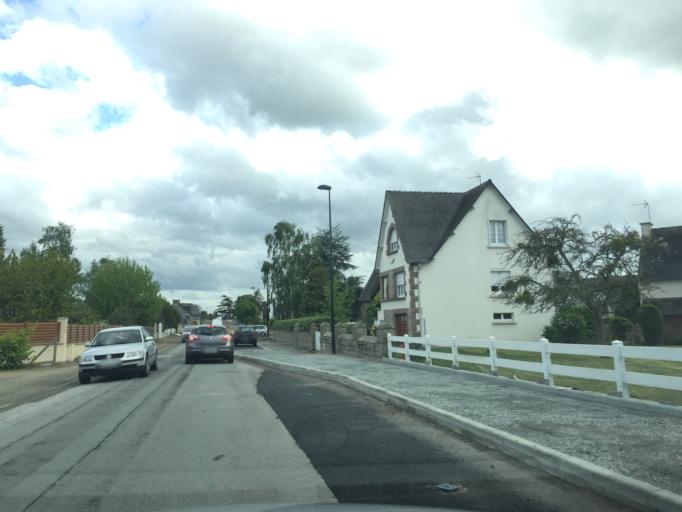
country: FR
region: Brittany
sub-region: Departement des Cotes-d'Armor
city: Ploubalay
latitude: 48.5837
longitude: -2.1434
